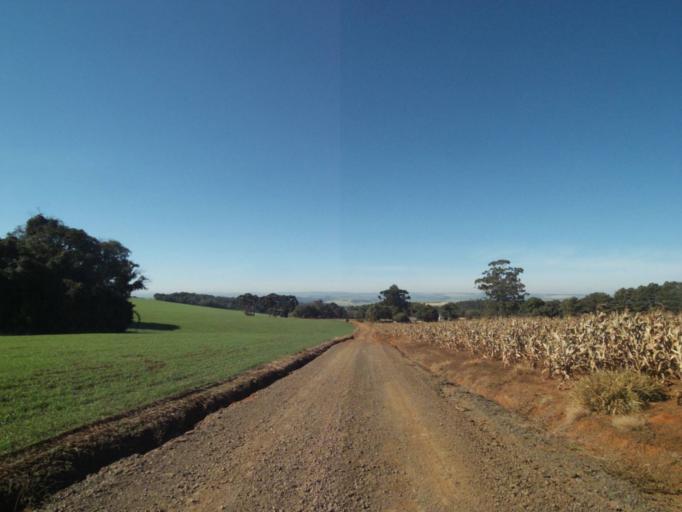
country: BR
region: Parana
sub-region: Tibagi
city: Tibagi
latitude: -24.3806
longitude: -50.3271
